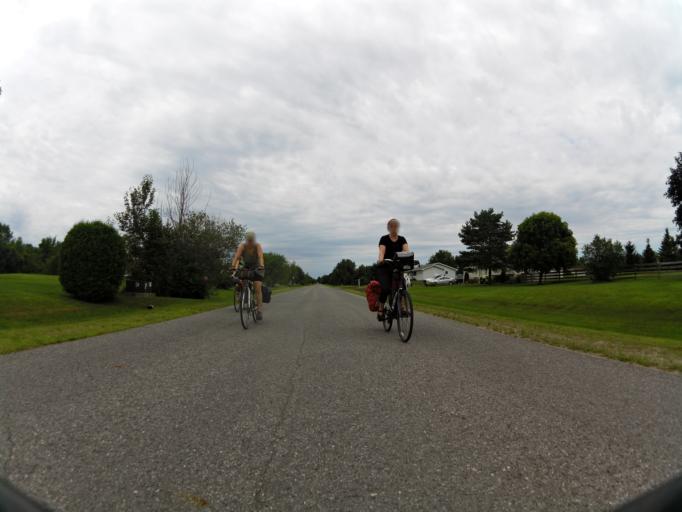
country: CA
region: Ontario
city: Bells Corners
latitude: 45.0227
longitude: -75.6918
